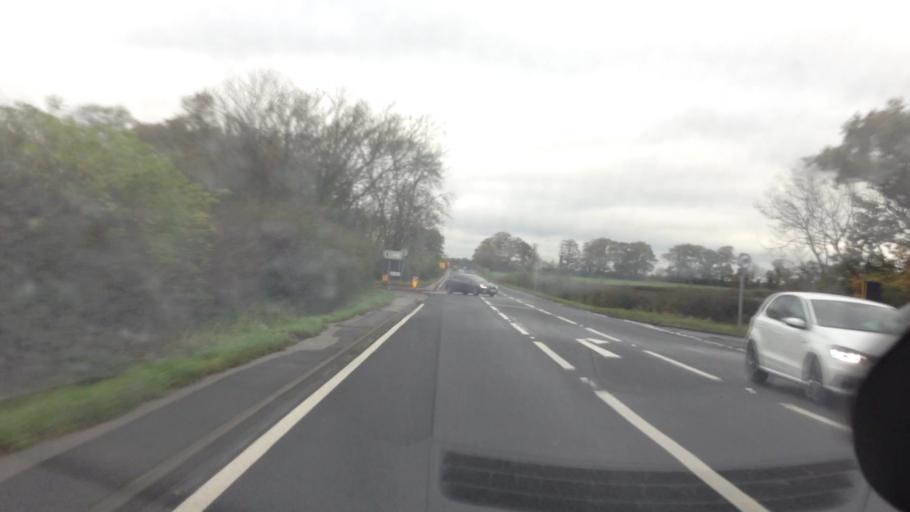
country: GB
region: England
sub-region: City and Borough of Leeds
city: Shadwell
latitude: 53.8493
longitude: -1.4647
